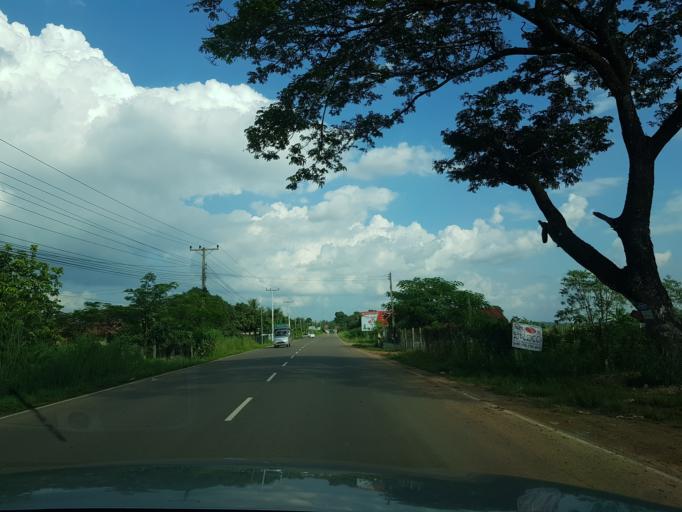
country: TH
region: Nong Khai
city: Pho Tak
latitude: 17.9804
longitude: 102.4581
